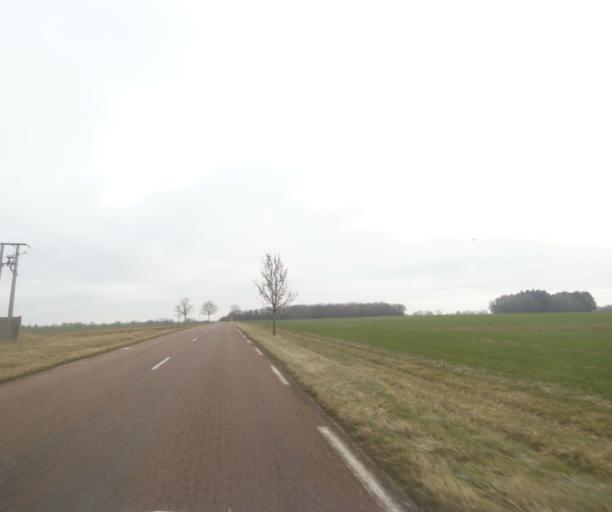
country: FR
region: Champagne-Ardenne
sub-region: Departement de la Haute-Marne
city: Chancenay
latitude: 48.6766
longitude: 5.0001
